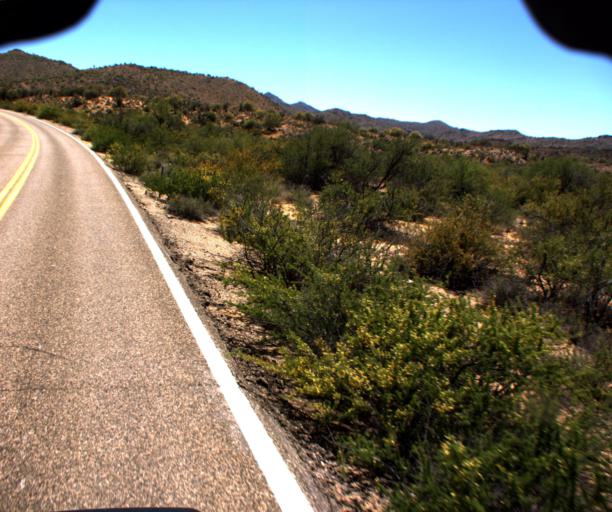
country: US
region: Arizona
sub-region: Yavapai County
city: Bagdad
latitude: 34.4717
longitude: -113.0529
